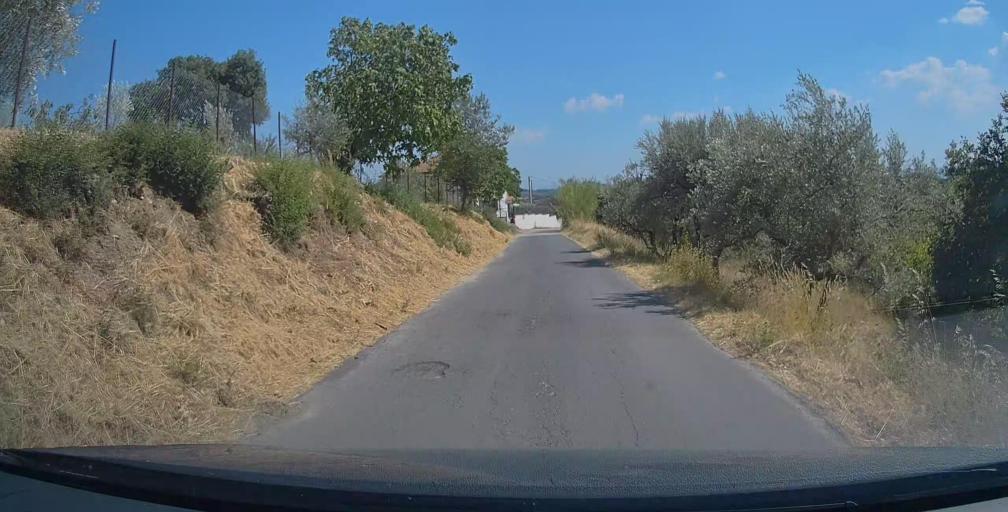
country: IT
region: Umbria
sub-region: Provincia di Terni
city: Calvi dell'Umbria
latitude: 42.3822
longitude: 12.5686
